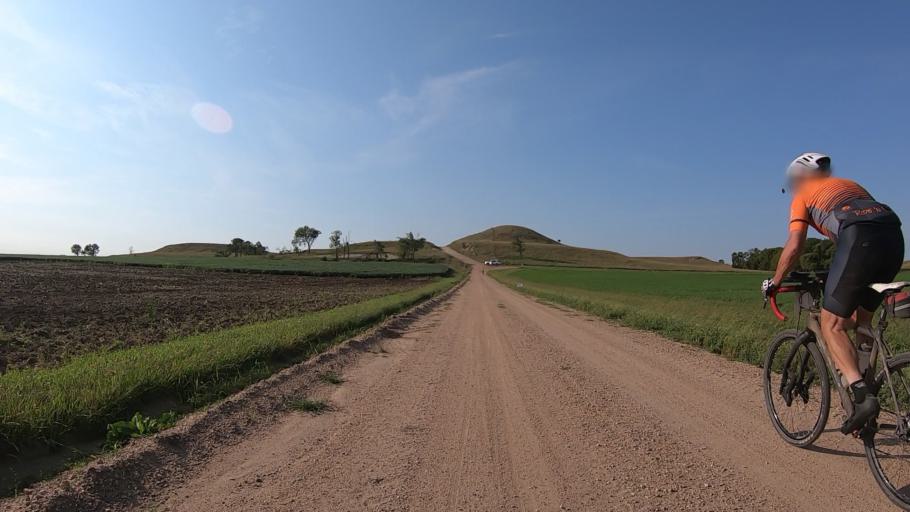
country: US
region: Kansas
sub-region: Marshall County
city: Blue Rapids
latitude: 39.6521
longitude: -96.8816
